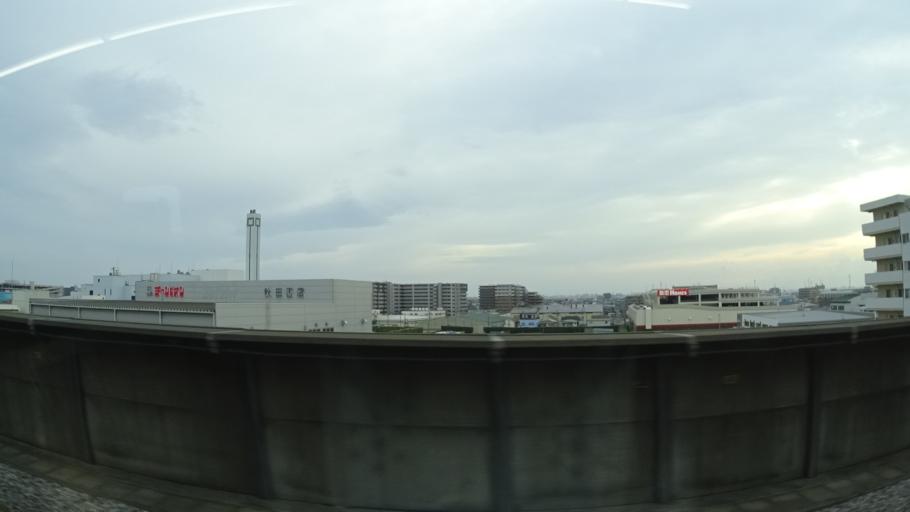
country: JP
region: Saitama
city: Shimotoda
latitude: 35.8345
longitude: 139.6530
